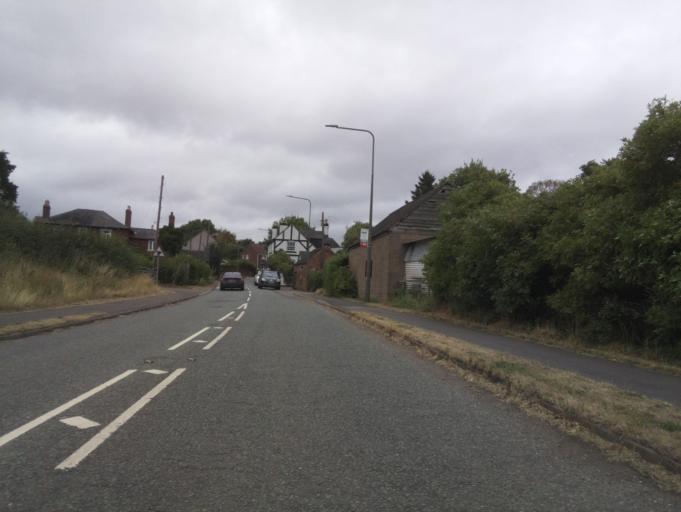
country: GB
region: England
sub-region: Derbyshire
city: Findern
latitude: 52.8688
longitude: -1.5449
